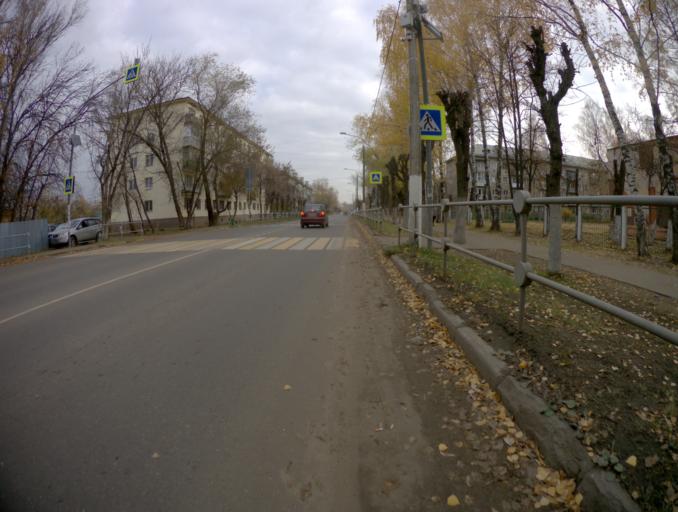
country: RU
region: Moskovskaya
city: Orekhovo-Zuyevo
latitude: 55.8014
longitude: 38.9610
